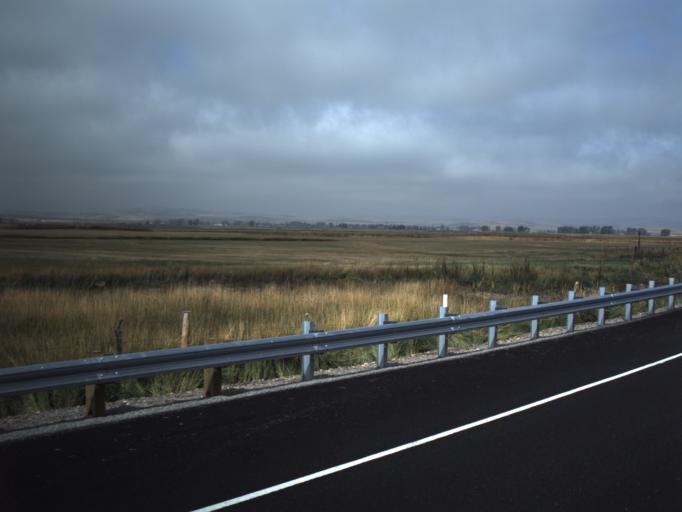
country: US
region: Utah
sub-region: Rich County
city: Randolph
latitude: 41.5025
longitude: -111.1237
